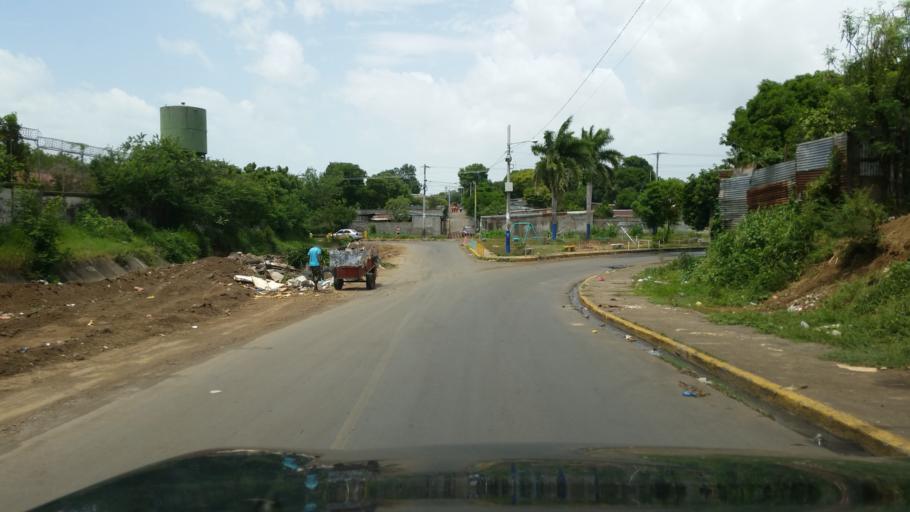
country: NI
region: Managua
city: Managua
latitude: 12.1339
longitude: -86.2128
